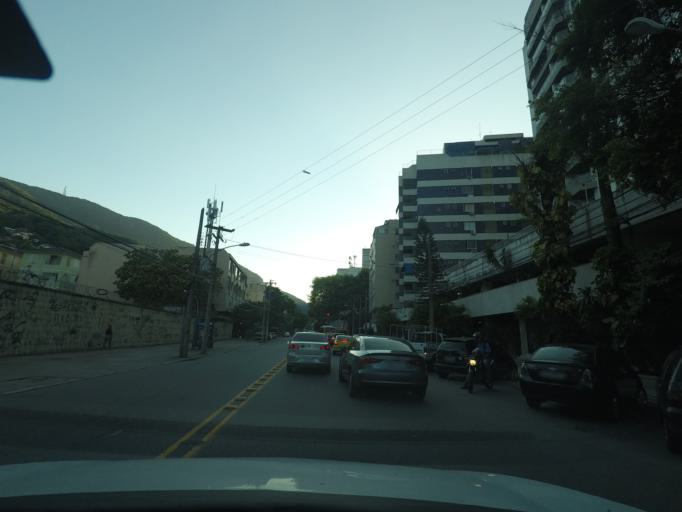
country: BR
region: Rio de Janeiro
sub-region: Rio De Janeiro
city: Rio de Janeiro
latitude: -22.9361
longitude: -43.2446
